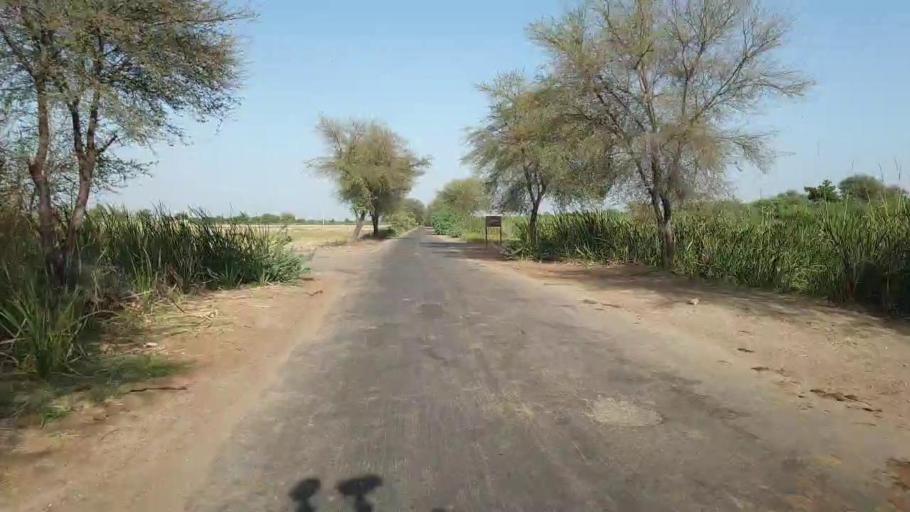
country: PK
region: Sindh
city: Nawabshah
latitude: 26.3726
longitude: 68.4716
